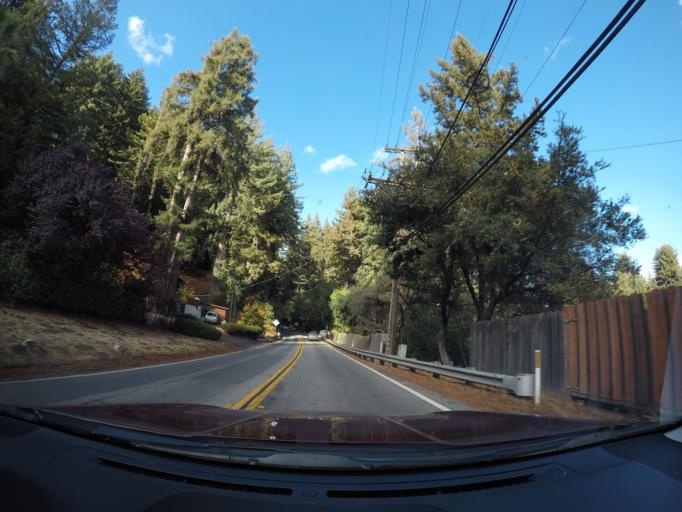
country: US
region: California
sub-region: Santa Cruz County
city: Ben Lomond
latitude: 37.0816
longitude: -122.0851
